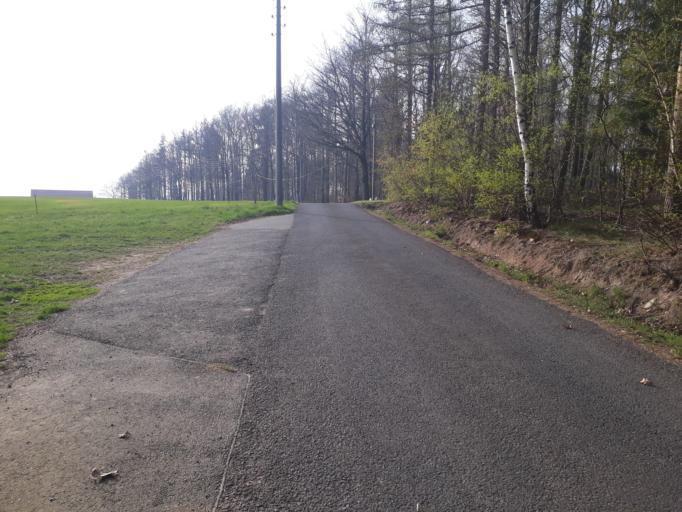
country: DE
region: Saxony
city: Reinhardtsgrimma
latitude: 50.8928
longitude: 13.7735
